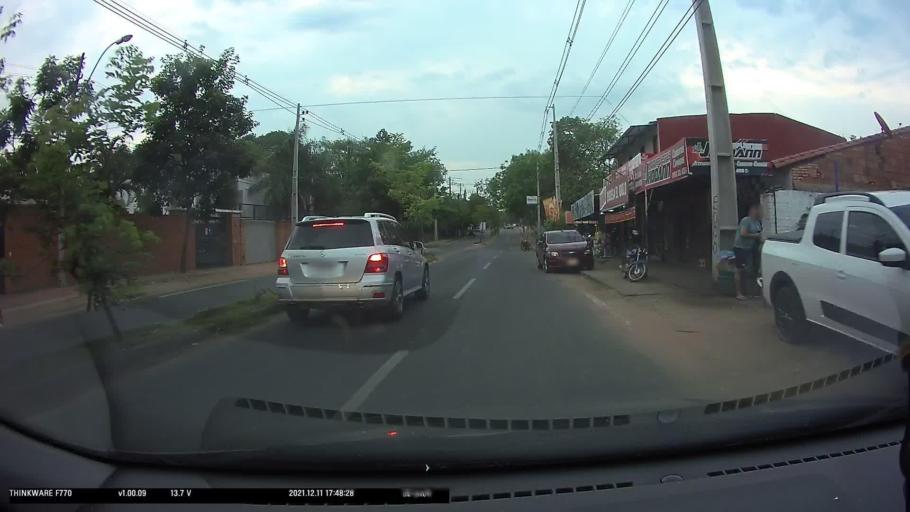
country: PY
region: Cordillera
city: San Bernardino
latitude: -25.3044
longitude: -57.2943
